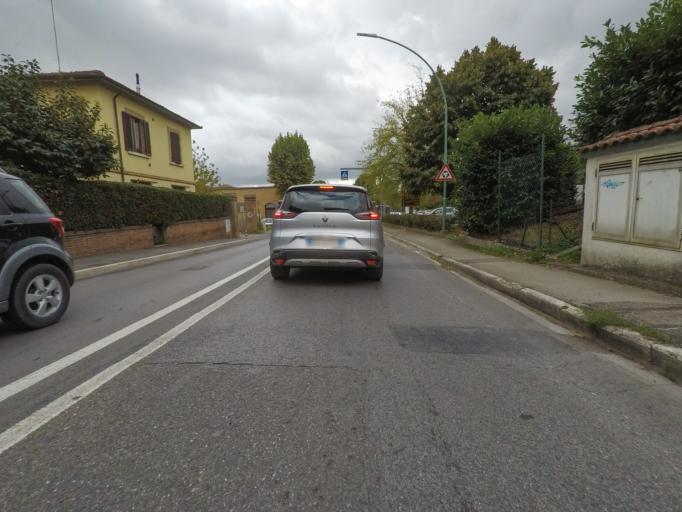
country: IT
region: Tuscany
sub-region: Provincia di Siena
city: Siena
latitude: 43.3175
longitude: 11.3539
